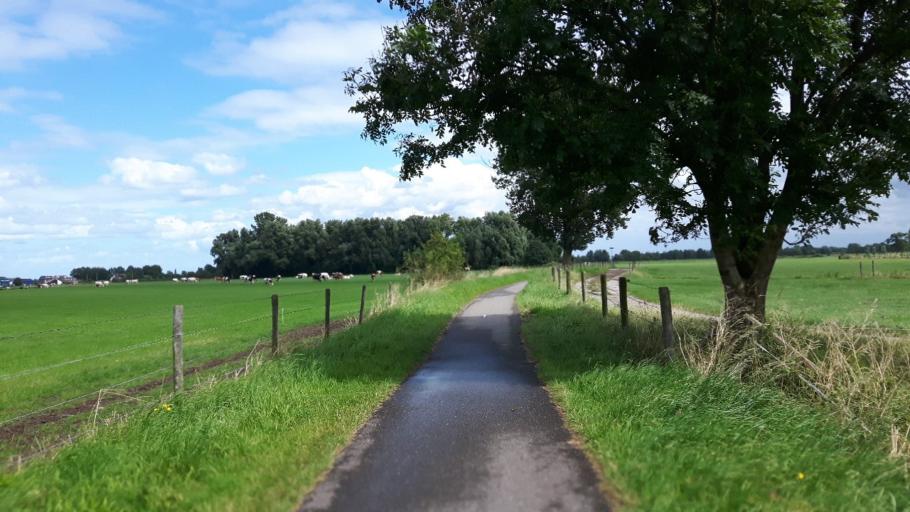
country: NL
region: Utrecht
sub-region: Gemeente Montfoort
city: Montfoort
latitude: 52.0505
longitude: 4.9989
